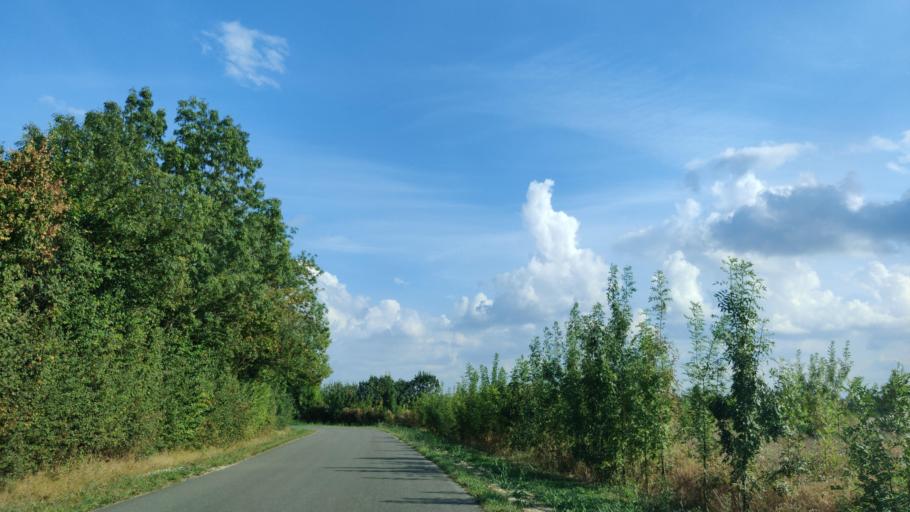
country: FR
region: Poitou-Charentes
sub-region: Departement des Deux-Sevres
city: Bessines
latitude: 46.2915
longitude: -0.5097
